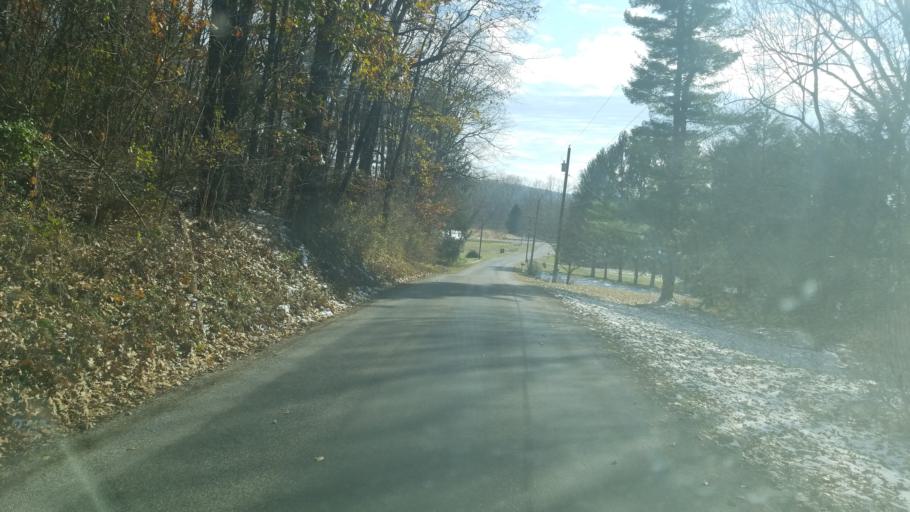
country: US
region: Ohio
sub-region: Licking County
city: Utica
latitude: 40.1643
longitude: -82.4256
